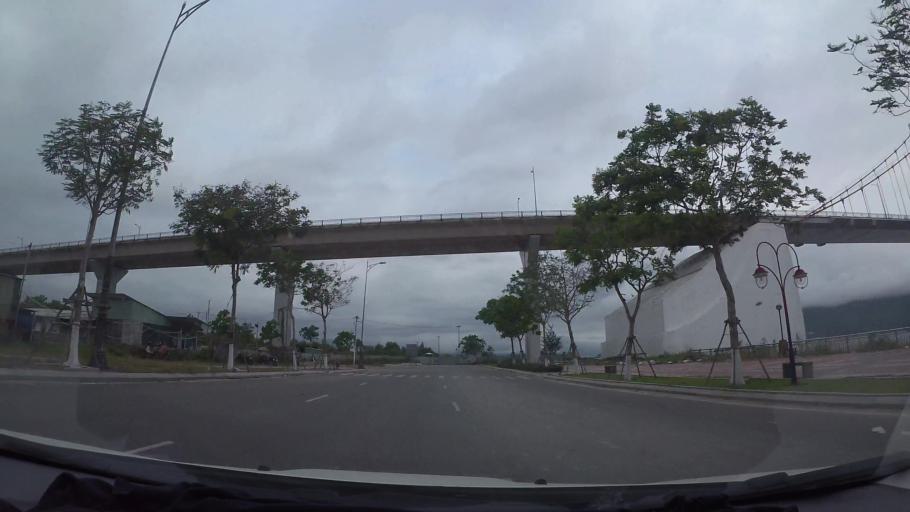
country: VN
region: Da Nang
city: Da Nang
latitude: 16.0929
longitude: 108.2175
